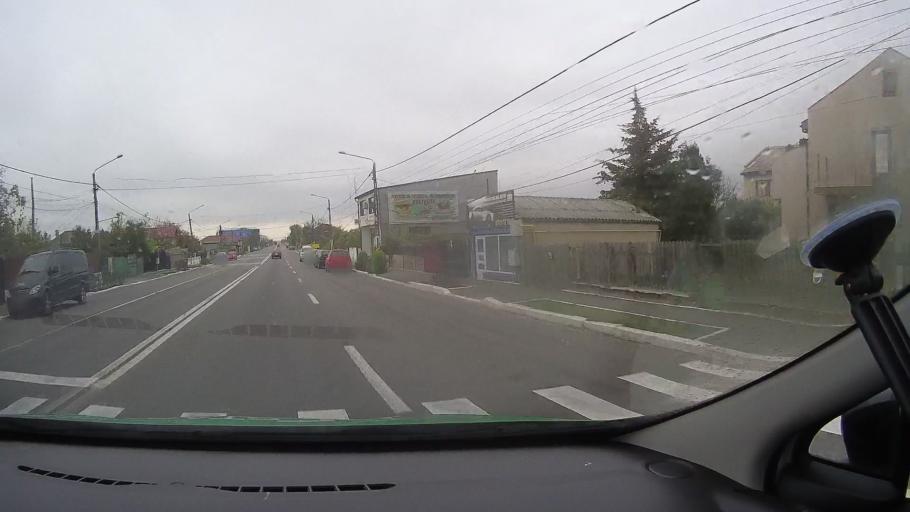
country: RO
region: Constanta
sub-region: Comuna Valu lui Traian
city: Valu lui Traian
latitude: 44.1653
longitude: 28.4680
